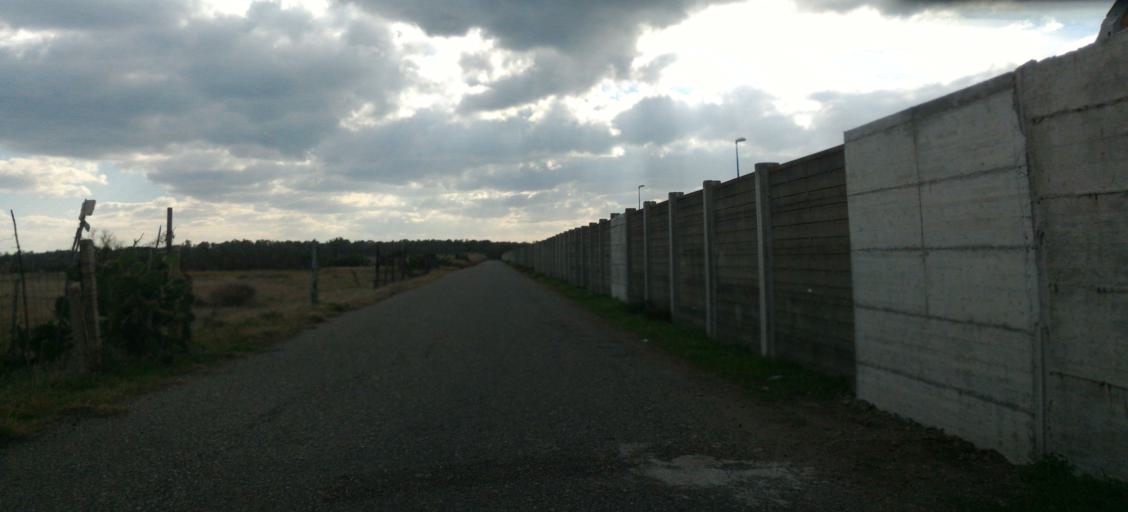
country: IT
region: Calabria
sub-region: Provincia di Crotone
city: Ciro Marina
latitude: 39.3996
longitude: 17.1446
